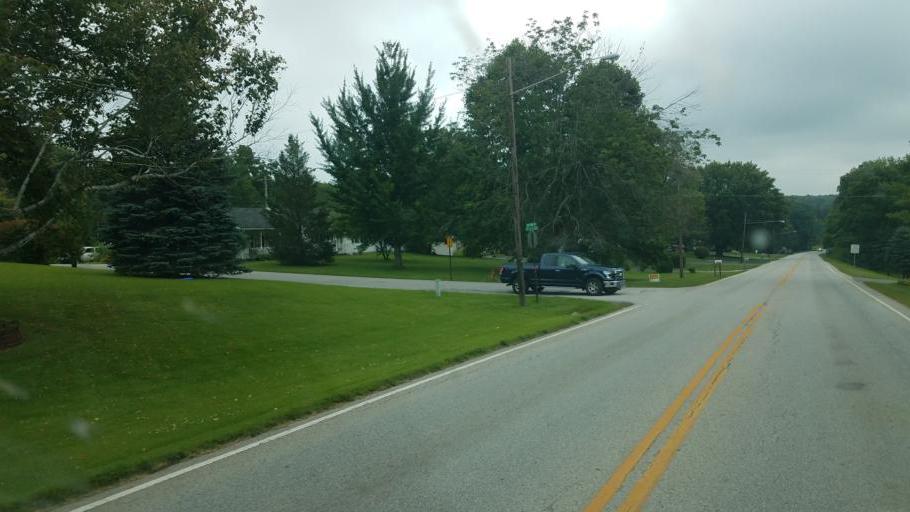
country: US
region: Ohio
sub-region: Highland County
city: Hillsboro
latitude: 39.2032
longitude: -83.5957
